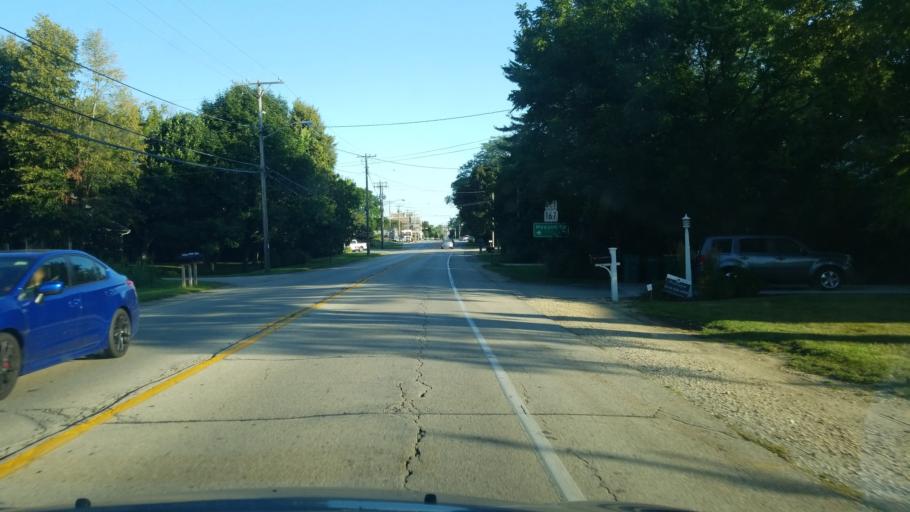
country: US
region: Wisconsin
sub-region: Ozaukee County
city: Mequon
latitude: 43.2188
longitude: -87.9810
